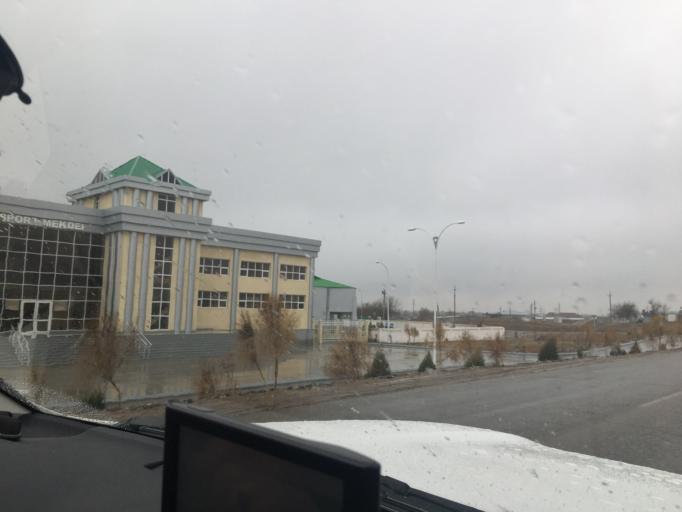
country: TM
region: Mary
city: Yoloeten
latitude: 37.2908
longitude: 62.3421
